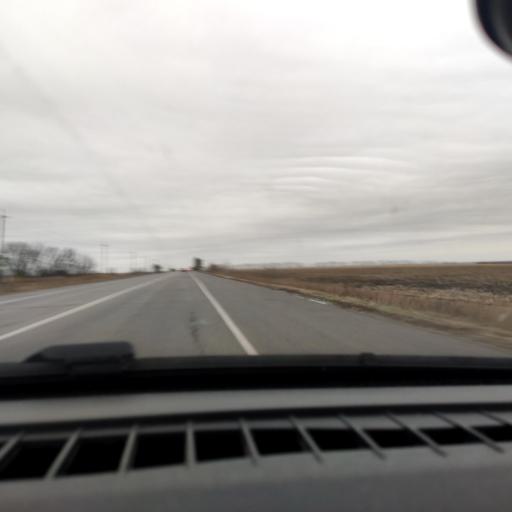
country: RU
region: Voronezj
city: Strelitsa
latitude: 51.5448
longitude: 38.9711
